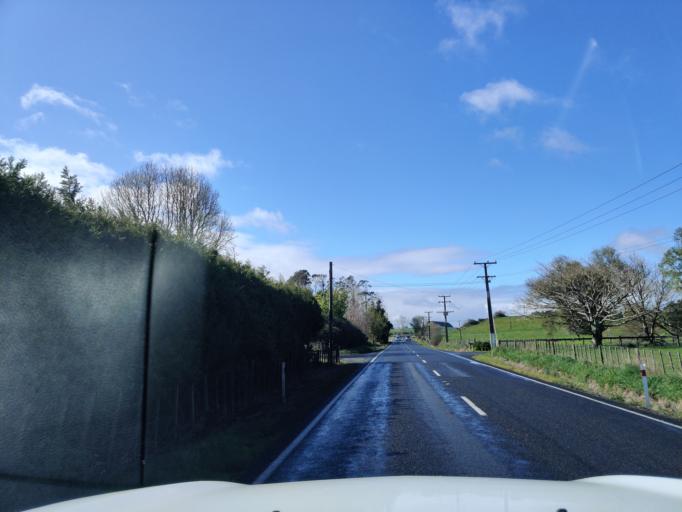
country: NZ
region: Waikato
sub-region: Otorohanga District
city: Otorohanga
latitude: -38.0740
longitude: 175.1799
